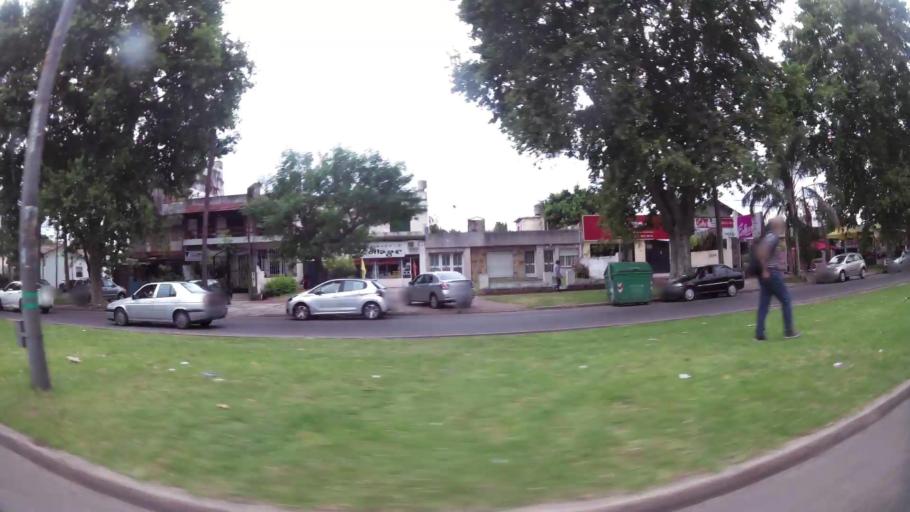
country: AR
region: Santa Fe
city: Granadero Baigorria
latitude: -32.8901
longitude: -60.6937
